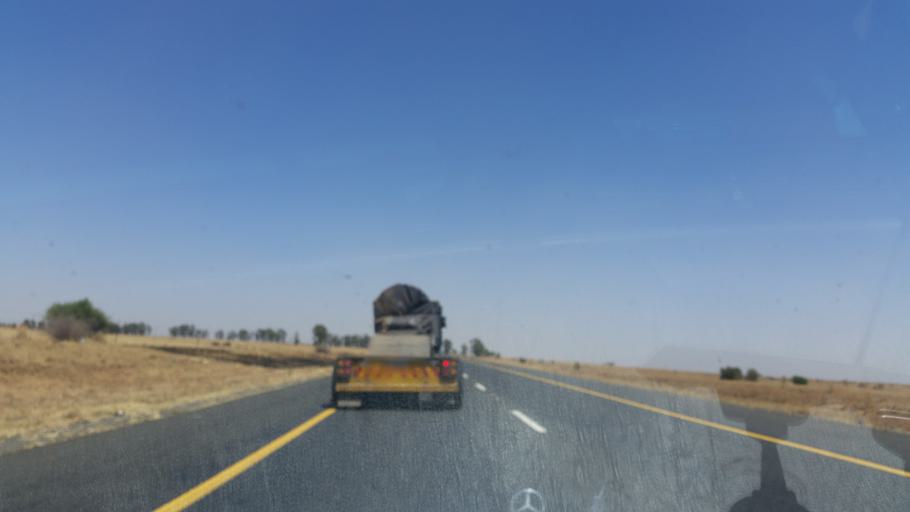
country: ZA
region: Orange Free State
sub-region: Lejweleputswa District Municipality
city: Winburg
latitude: -28.6366
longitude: 26.8962
